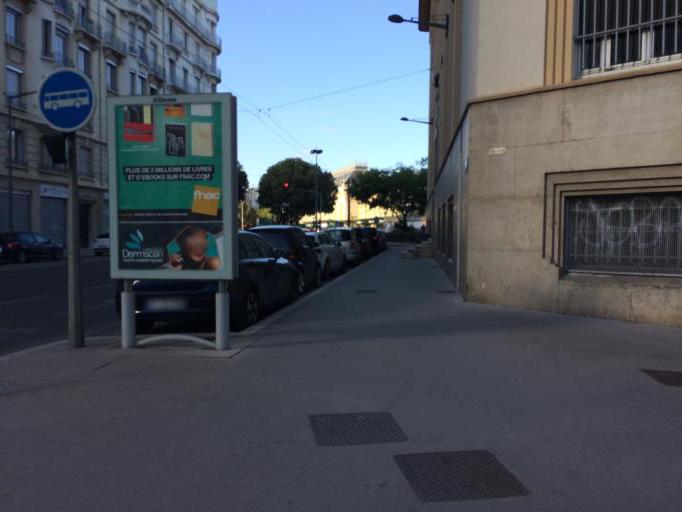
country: FR
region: Rhone-Alpes
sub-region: Departement du Rhone
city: Lyon
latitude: 45.7653
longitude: 4.8590
